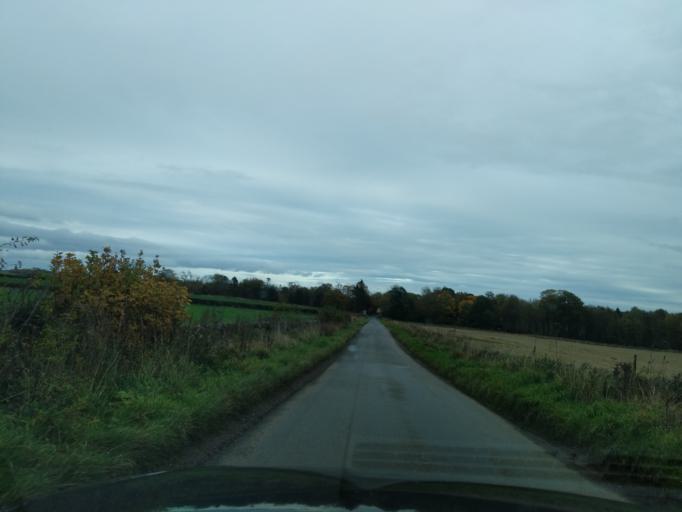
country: GB
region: Scotland
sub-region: Fife
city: Saint Andrews
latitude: 56.2881
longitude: -2.7799
